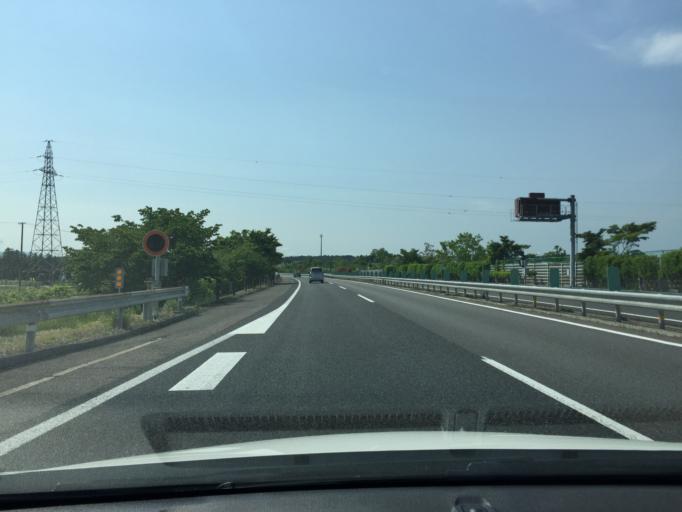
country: JP
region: Fukushima
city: Koriyama
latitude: 37.3640
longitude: 140.3122
